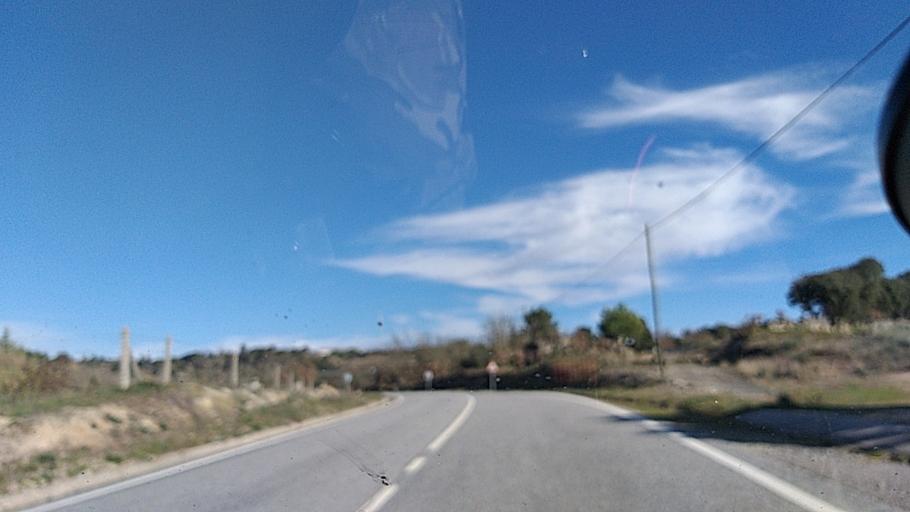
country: ES
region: Castille and Leon
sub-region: Provincia de Salamanca
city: Fuentes de Onoro
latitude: 40.6141
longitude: -6.8920
